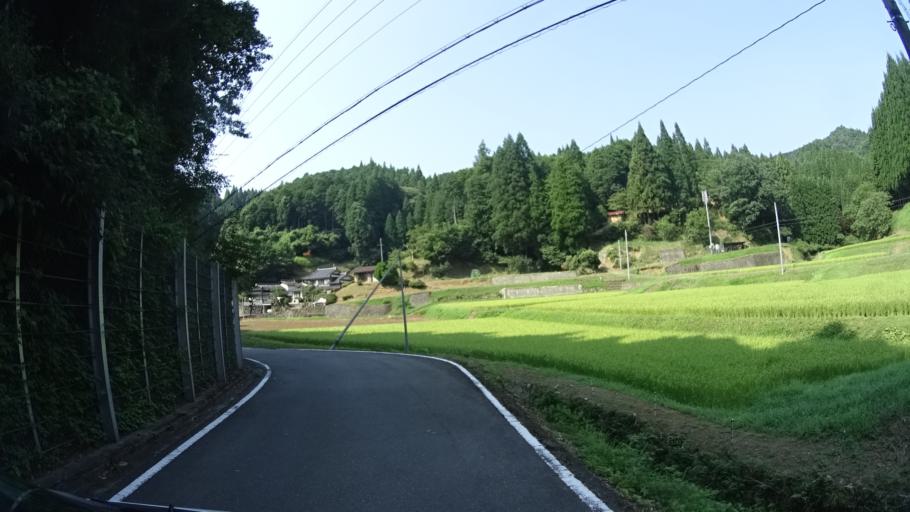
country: JP
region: Kyoto
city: Ayabe
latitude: 35.4016
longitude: 135.2139
